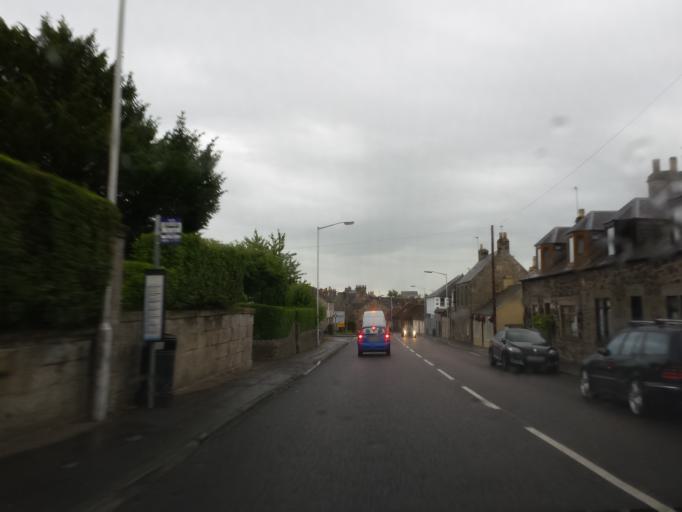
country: GB
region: Scotland
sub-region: Fife
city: Leuchars
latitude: 56.3837
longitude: -2.8894
